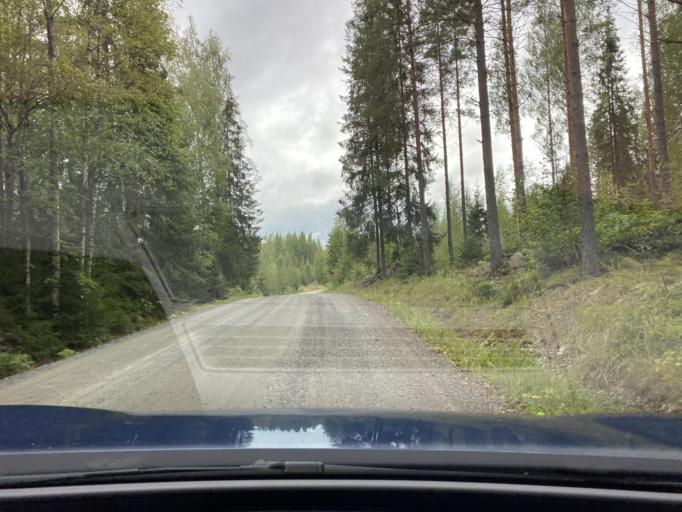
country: FI
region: Pirkanmaa
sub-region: Lounais-Pirkanmaa
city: Vammala
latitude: 61.2586
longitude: 23.0142
